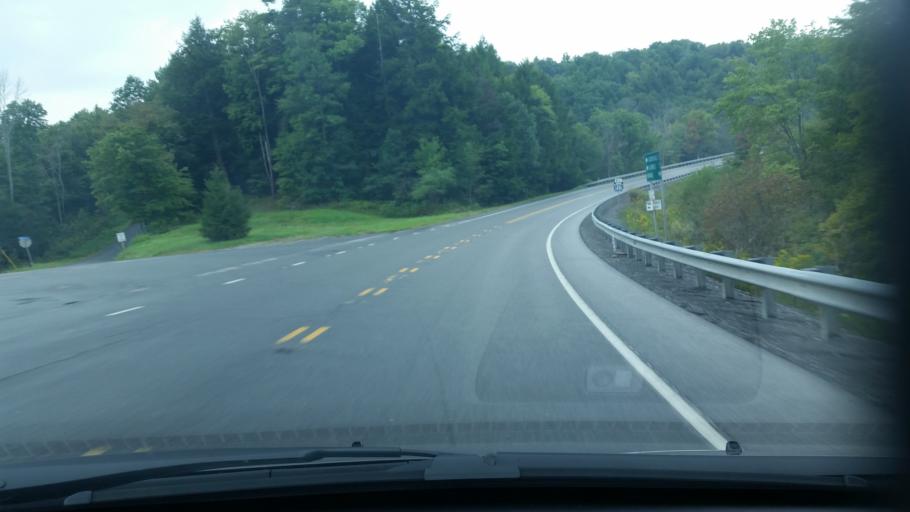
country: US
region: Pennsylvania
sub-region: Clearfield County
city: Shiloh
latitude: 41.0873
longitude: -78.2455
